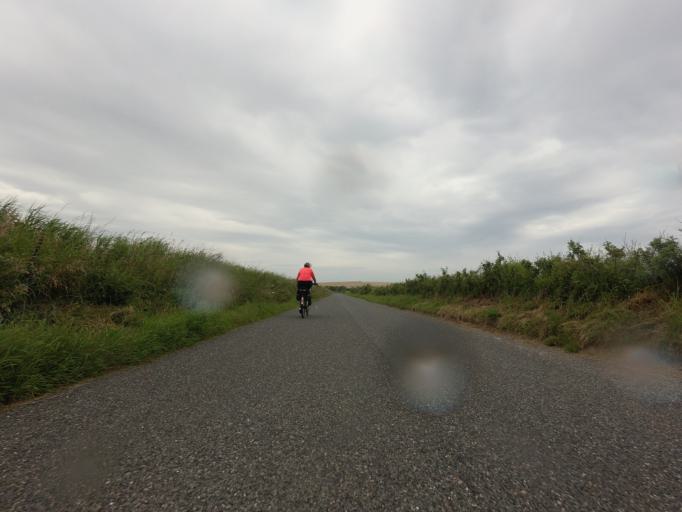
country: GB
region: Scotland
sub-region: Aberdeenshire
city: Portsoy
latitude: 57.6735
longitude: -2.6421
